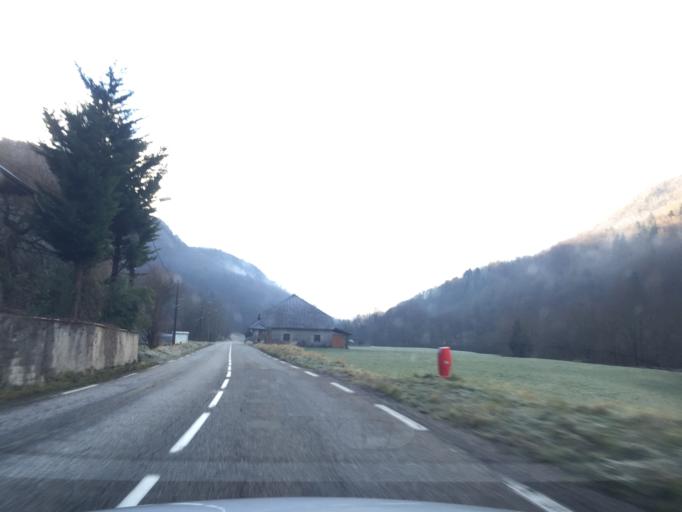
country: FR
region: Rhone-Alpes
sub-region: Departement de la Haute-Savoie
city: Gruffy
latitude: 45.7397
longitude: 6.0981
